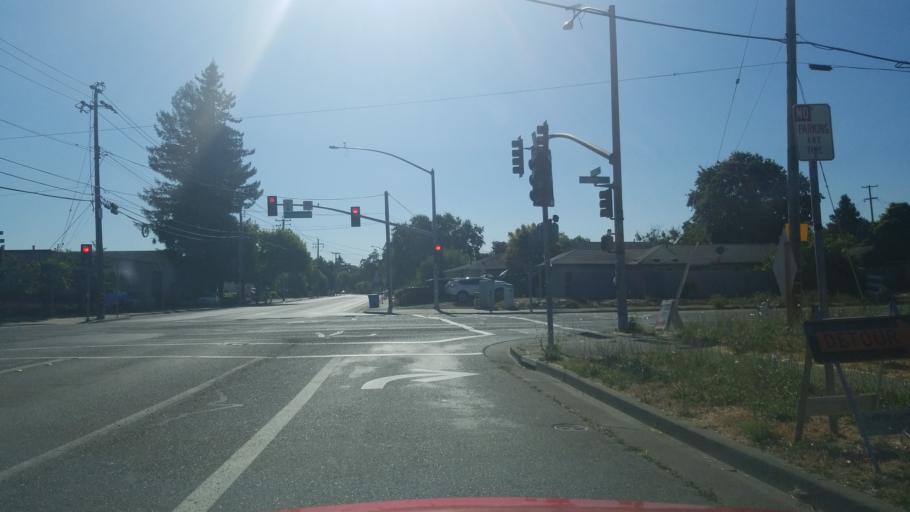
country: US
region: California
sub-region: Sonoma County
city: Santa Rosa
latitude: 38.4416
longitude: -122.7293
